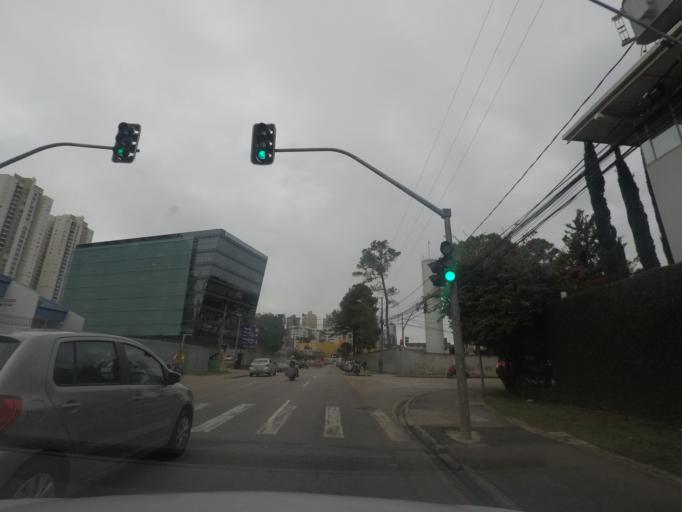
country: BR
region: Parana
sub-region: Curitiba
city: Curitiba
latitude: -25.4384
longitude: -49.2422
